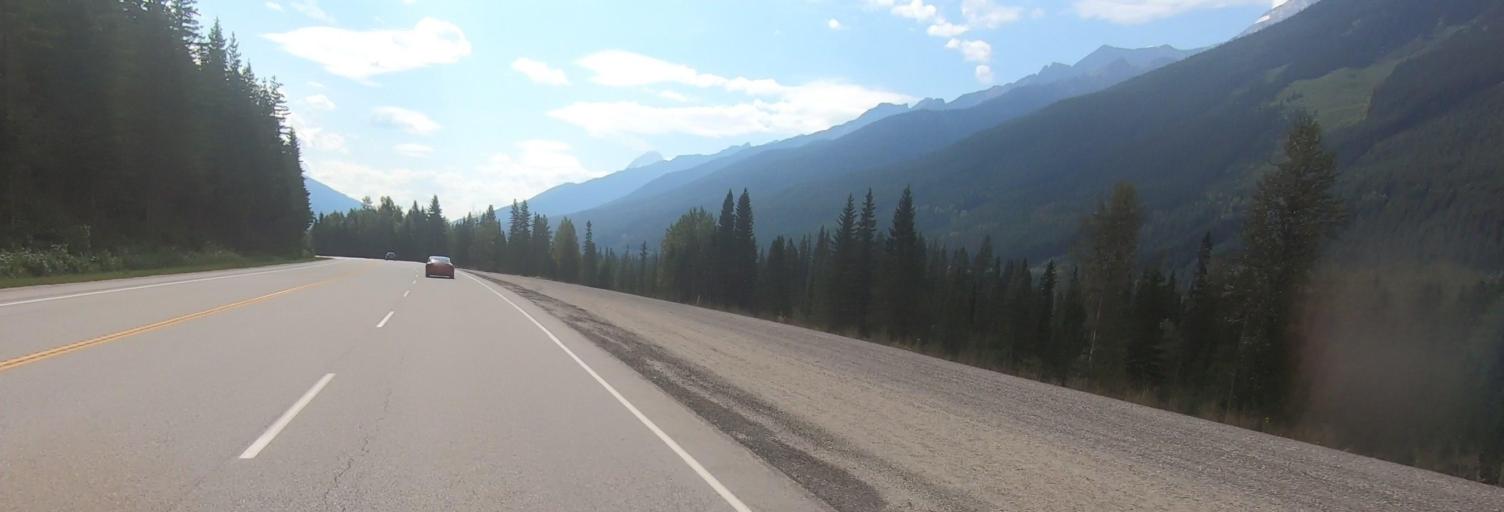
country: CA
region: British Columbia
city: Golden
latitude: 51.4071
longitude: -117.4701
